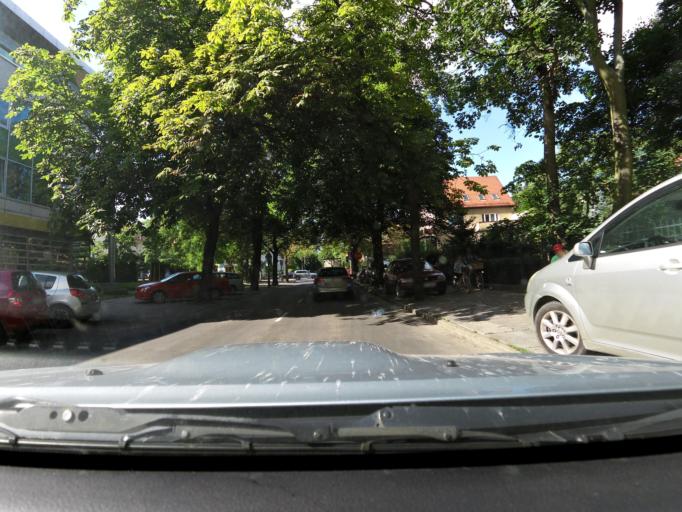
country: PL
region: Pomeranian Voivodeship
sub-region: Sopot
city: Sopot
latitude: 54.4356
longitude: 18.5688
